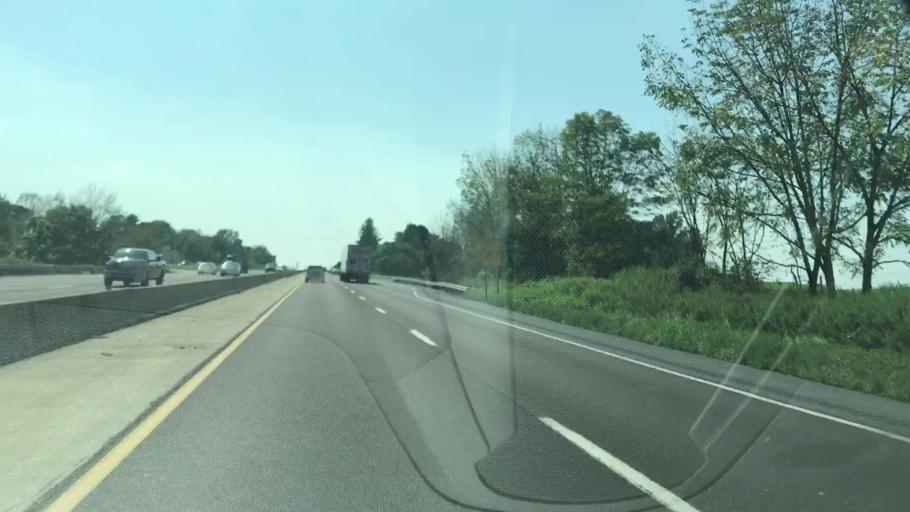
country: US
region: Pennsylvania
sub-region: Lebanon County
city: Myerstown
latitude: 40.4839
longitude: -76.2562
